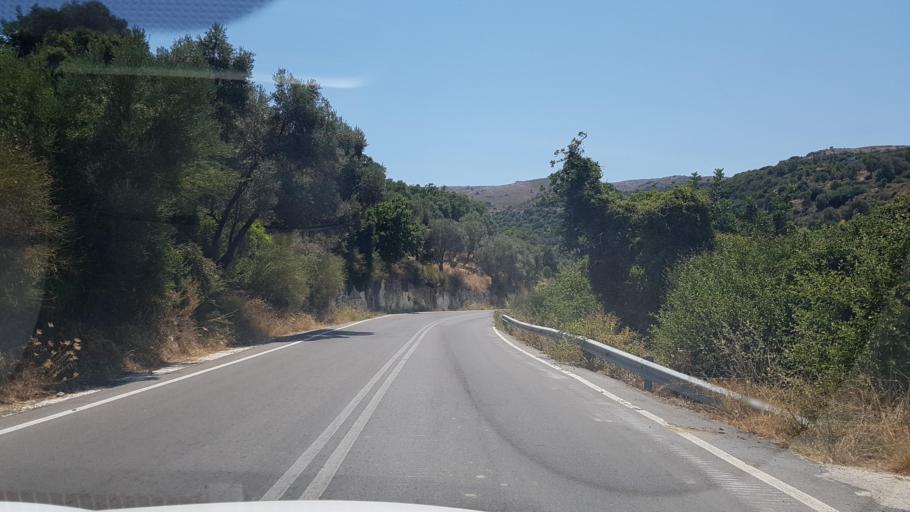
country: GR
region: Crete
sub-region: Nomos Rethymnis
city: Agia Foteini
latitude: 35.3366
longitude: 24.6104
